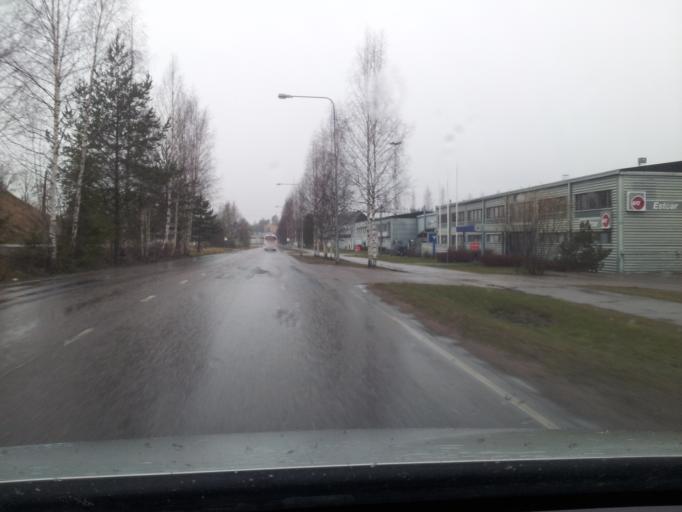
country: FI
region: Uusimaa
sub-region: Helsinki
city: Espoo
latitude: 60.1859
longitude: 24.6120
